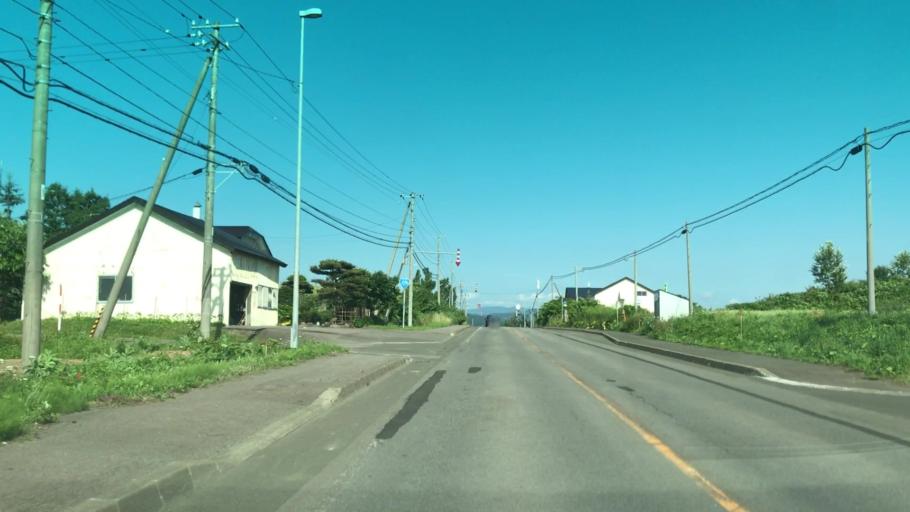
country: JP
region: Hokkaido
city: Iwanai
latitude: 42.9803
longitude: 140.5955
